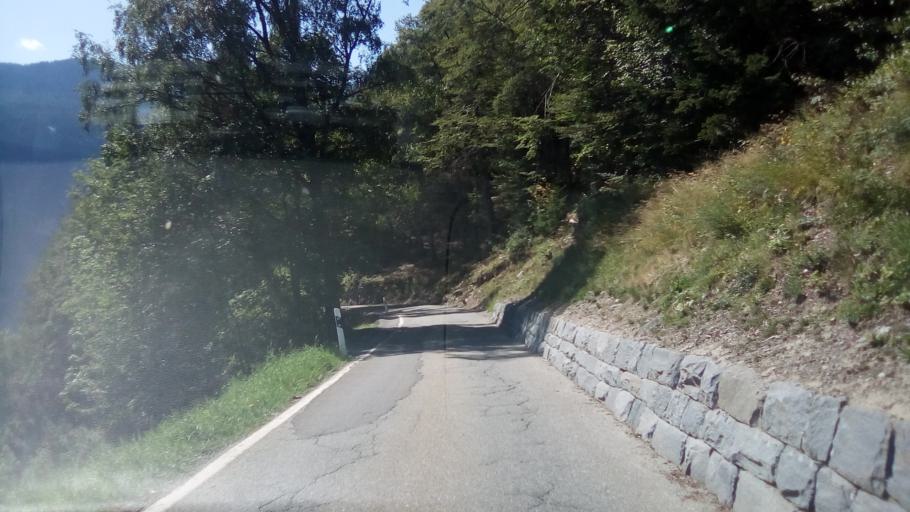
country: CH
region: Valais
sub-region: Saint-Maurice District
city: Salvan
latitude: 46.1255
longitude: 7.0191
